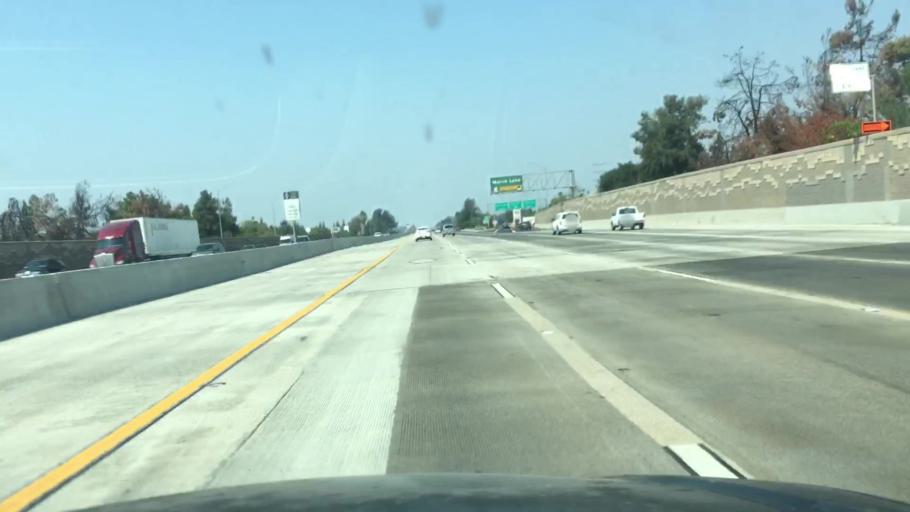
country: US
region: California
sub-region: San Joaquin County
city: Country Club
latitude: 37.9778
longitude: -121.3432
